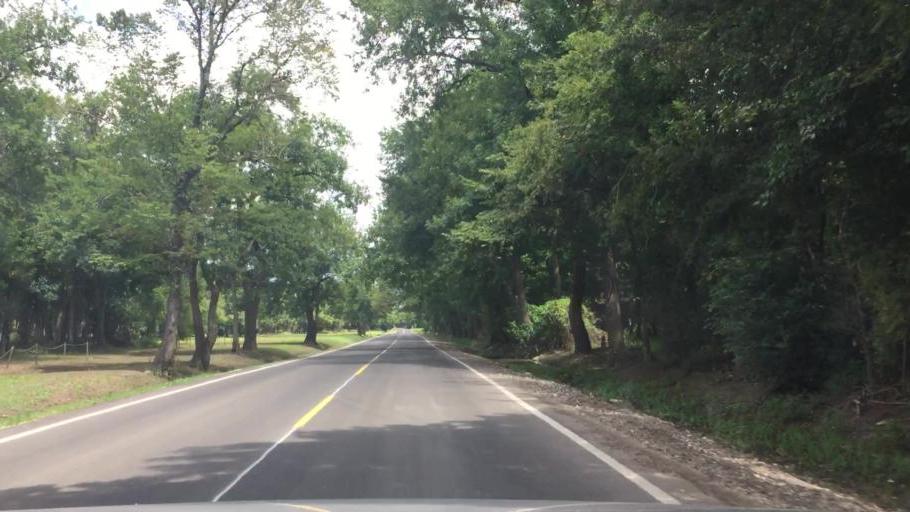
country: US
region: Texas
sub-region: Harris County
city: Jersey Village
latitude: 29.8133
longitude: -95.6377
